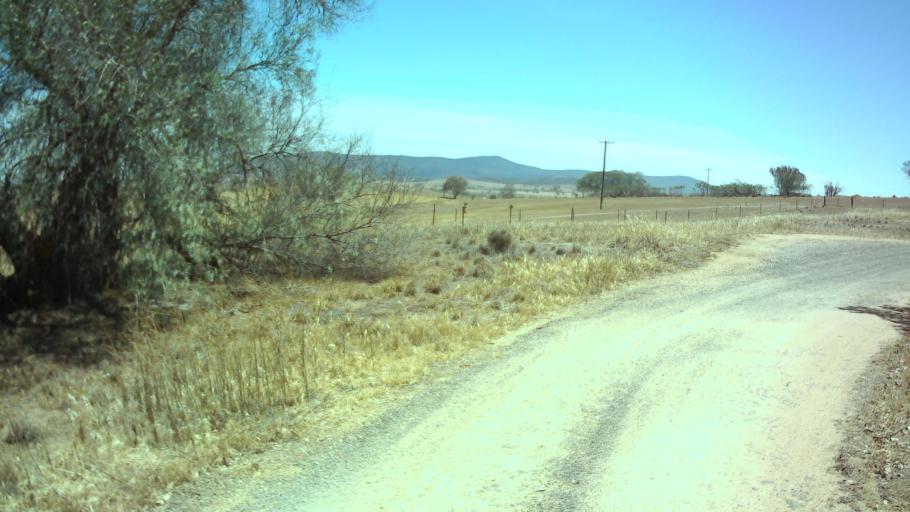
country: AU
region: New South Wales
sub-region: Weddin
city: Grenfell
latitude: -33.9312
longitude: 148.1534
